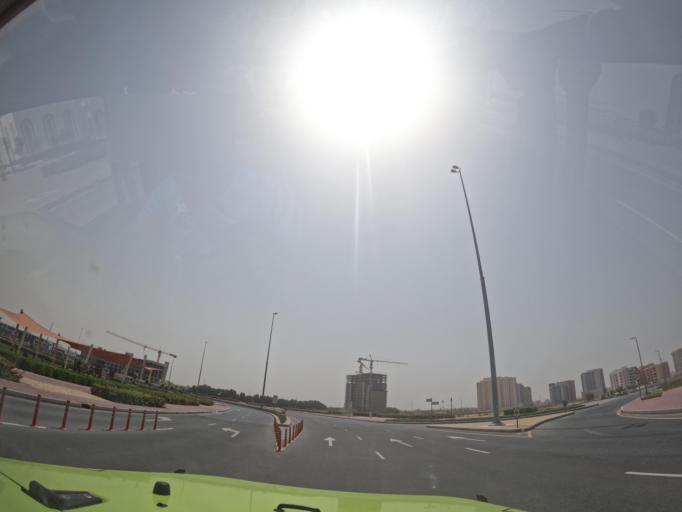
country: AE
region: Dubai
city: Dubai
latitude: 25.0924
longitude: 55.3787
